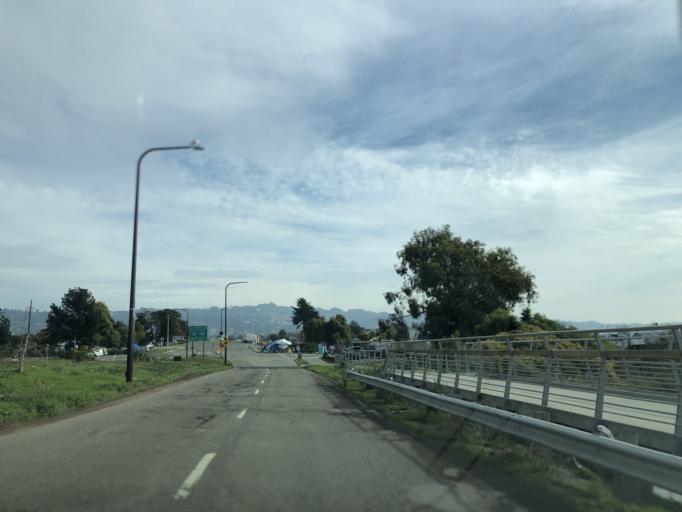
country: US
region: California
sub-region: Alameda County
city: Albany
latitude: 37.8659
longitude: -122.3070
